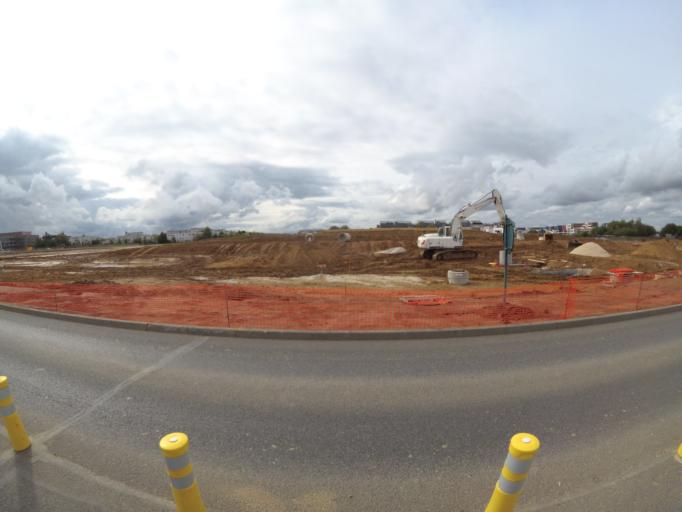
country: FR
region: Ile-de-France
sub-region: Departement de Seine-et-Marne
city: Montevrain
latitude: 48.8588
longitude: 2.7673
